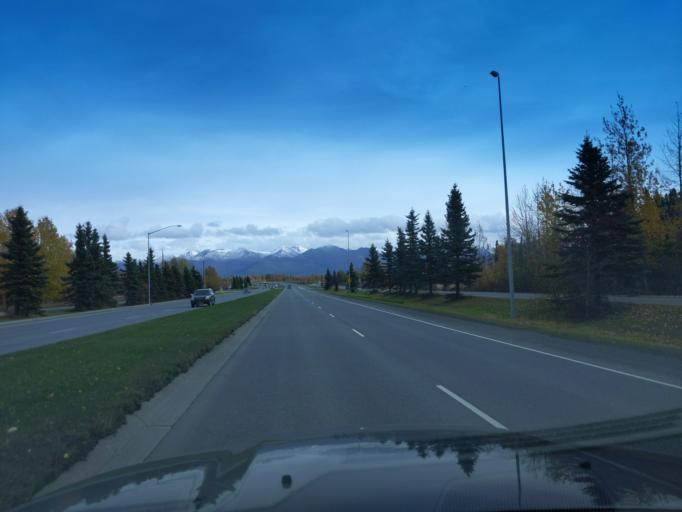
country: US
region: Alaska
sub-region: Anchorage Municipality
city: Anchorage
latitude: 61.1731
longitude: -149.9323
